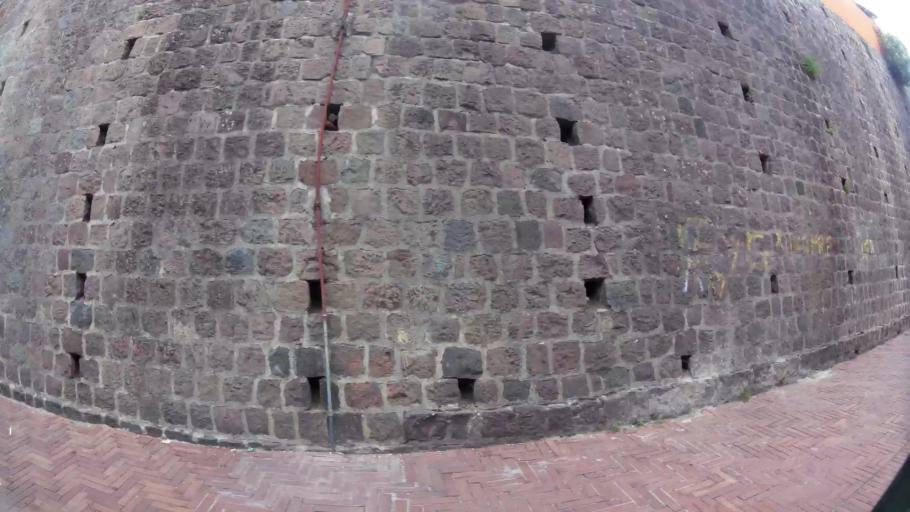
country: EC
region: Pichincha
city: Quito
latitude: -0.2175
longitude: -78.5163
